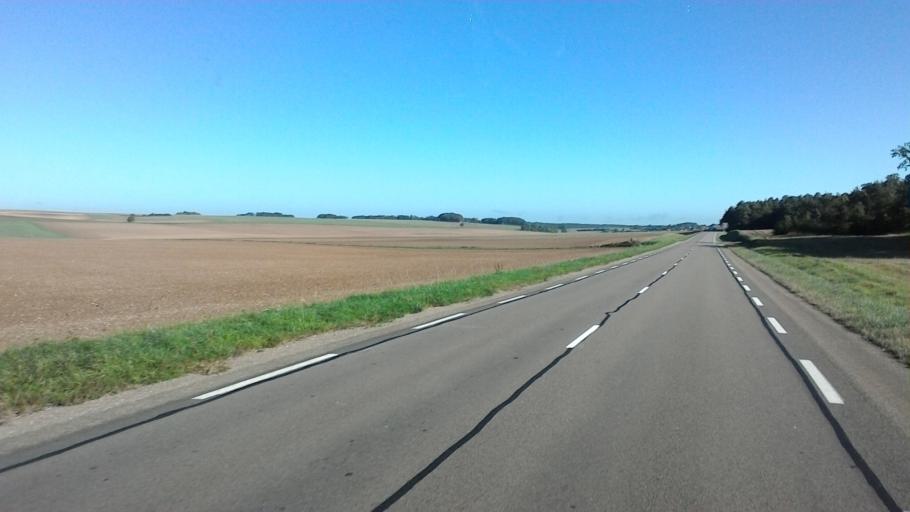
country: FR
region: Bourgogne
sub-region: Departement de la Cote-d'Or
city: Chatillon-sur-Seine
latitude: 47.7936
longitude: 4.5175
